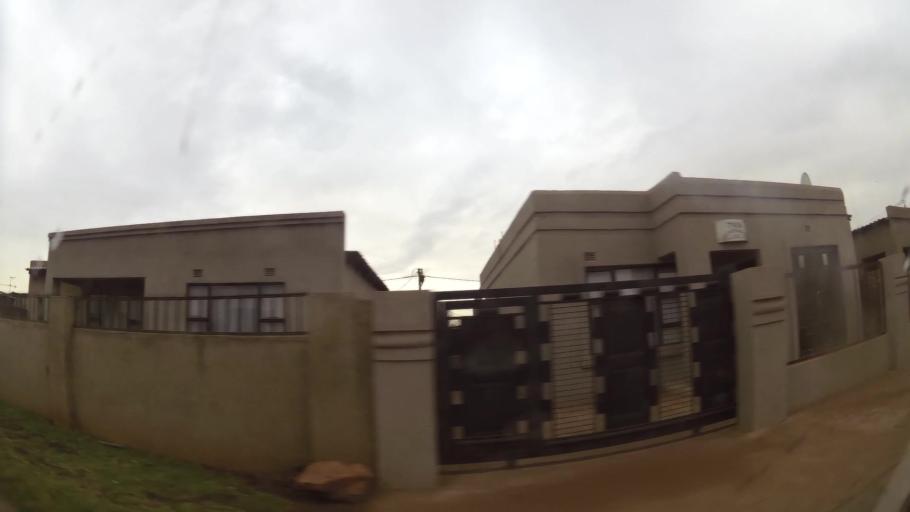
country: ZA
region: Gauteng
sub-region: Ekurhuleni Metropolitan Municipality
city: Germiston
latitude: -26.3817
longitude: 28.1773
